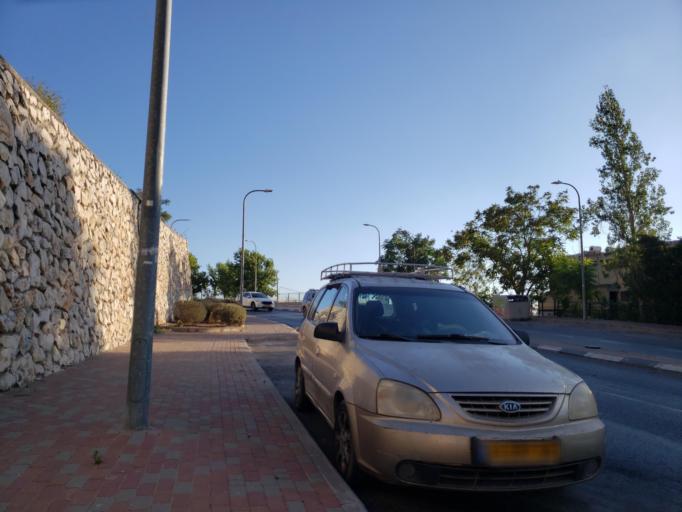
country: IL
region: Northern District
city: Safed
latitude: 32.9622
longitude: 35.4901
